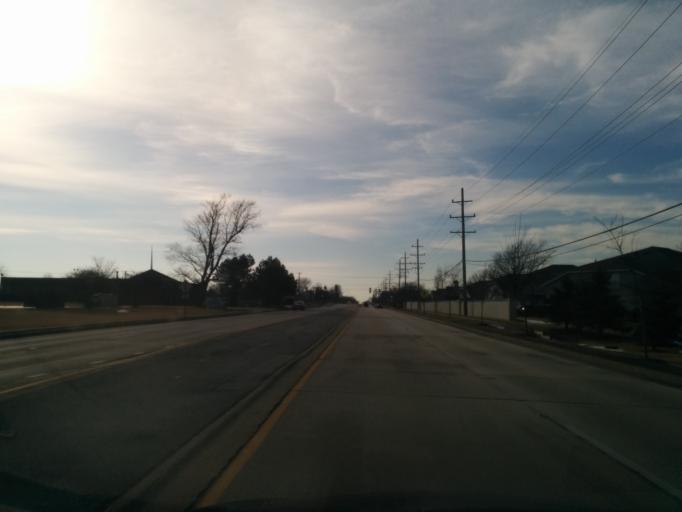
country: US
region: Illinois
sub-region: Cook County
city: Orland Hills
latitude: 41.5800
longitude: -87.8201
